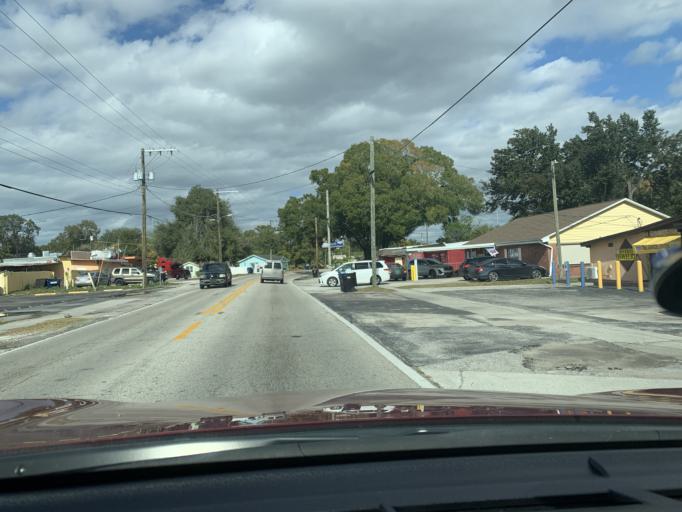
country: US
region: Florida
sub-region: Hillsborough County
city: Egypt Lake-Leto
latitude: 28.0148
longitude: -82.4853
